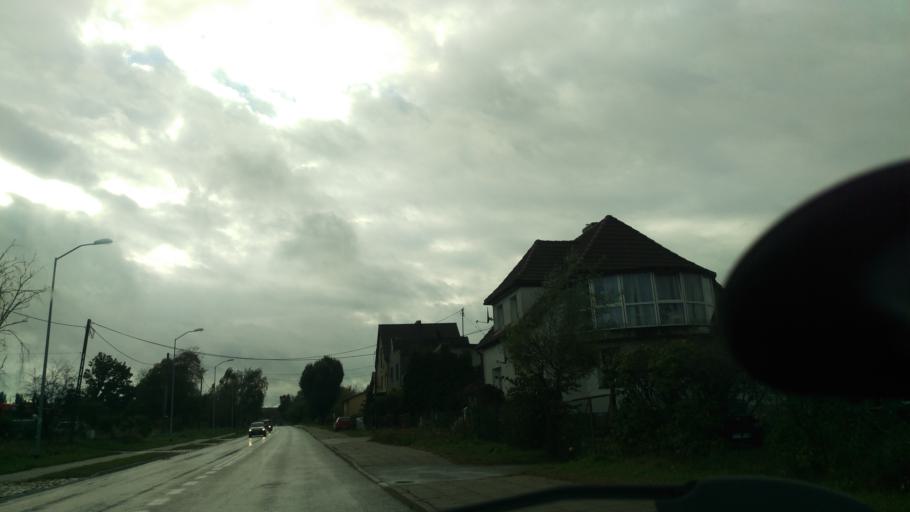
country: PL
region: West Pomeranian Voivodeship
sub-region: Szczecin
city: Szczecin
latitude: 53.3718
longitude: 14.6734
